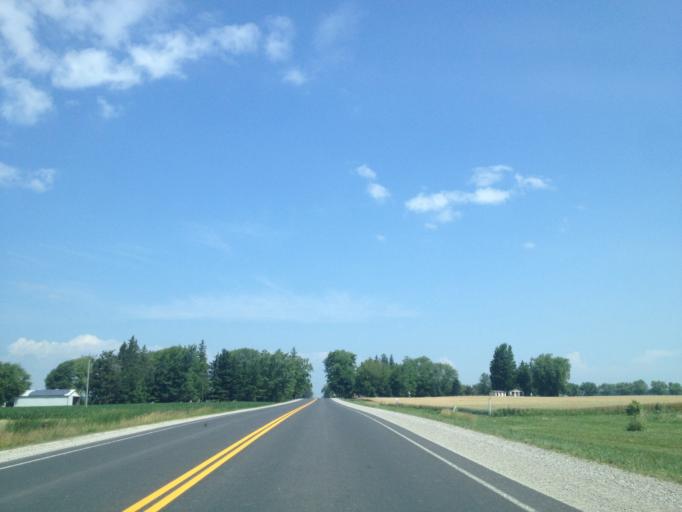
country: CA
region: Ontario
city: Stratford
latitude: 43.3132
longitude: -81.2016
